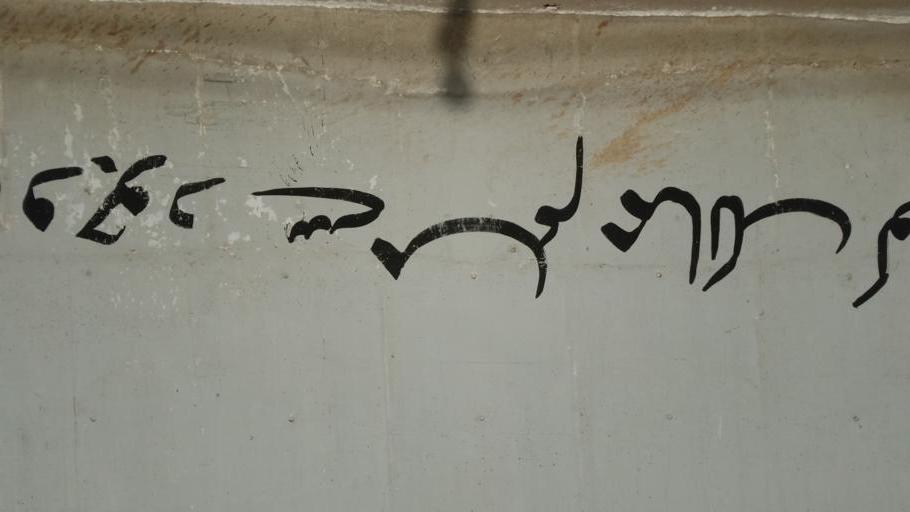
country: PK
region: Sindh
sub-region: Karachi District
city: Karachi
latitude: 24.8783
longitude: 67.0387
